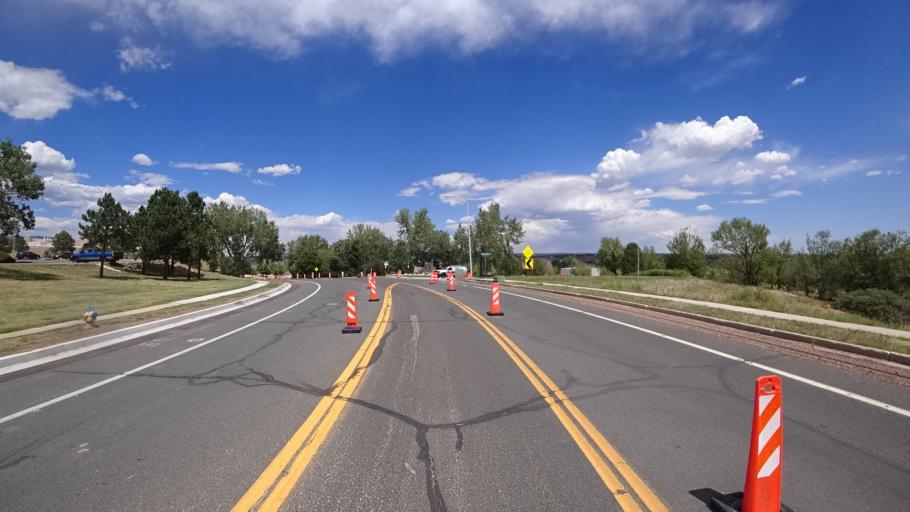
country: US
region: Colorado
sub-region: El Paso County
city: Stratmoor
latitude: 38.7873
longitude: -104.8041
